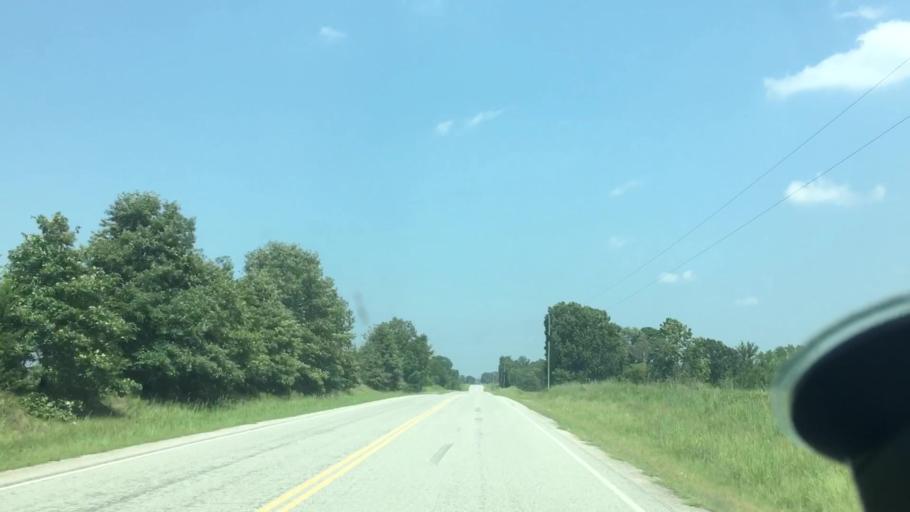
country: US
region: Oklahoma
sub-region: Atoka County
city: Atoka
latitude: 34.2667
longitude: -95.9361
